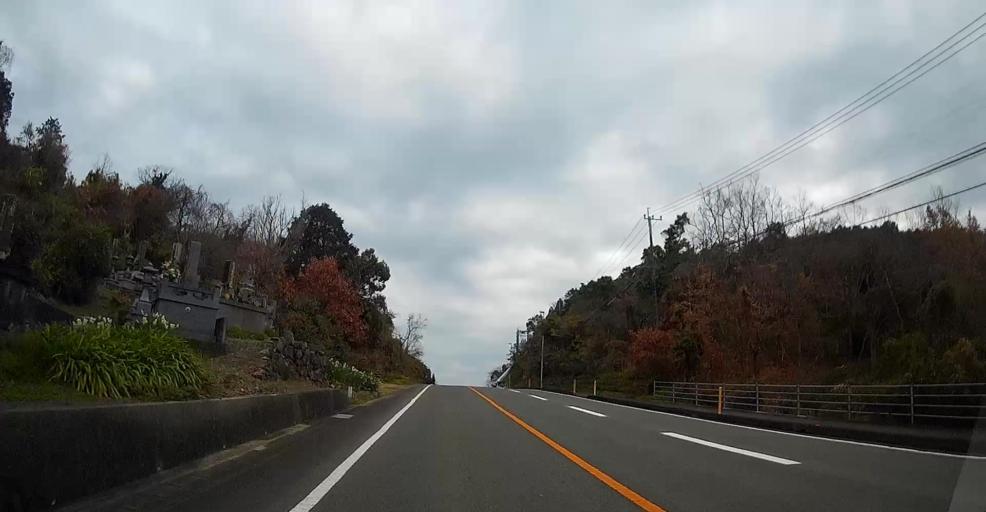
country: JP
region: Kumamoto
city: Hondo
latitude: 32.4647
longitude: 130.2407
